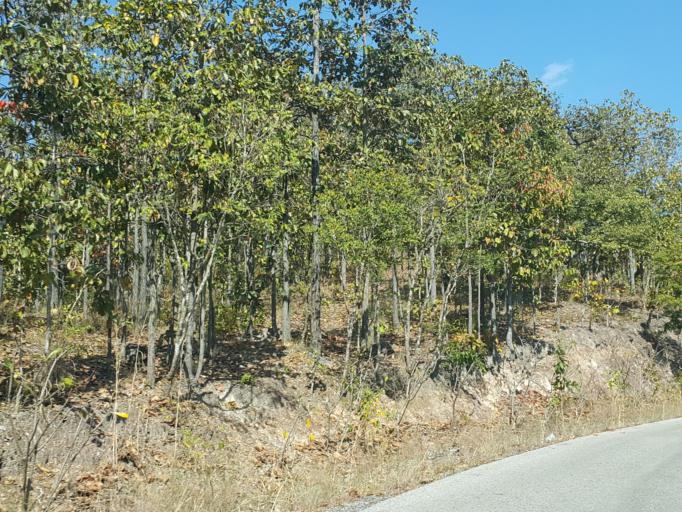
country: TH
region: Chiang Mai
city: Mae Taeng
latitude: 19.0328
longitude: 98.9946
